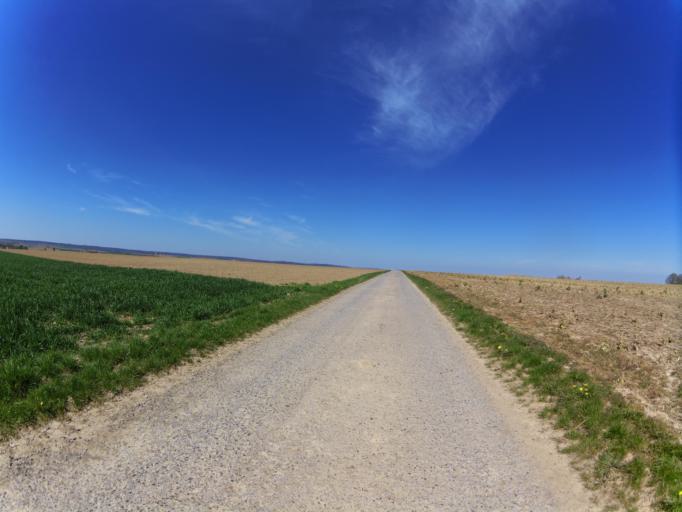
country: DE
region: Bavaria
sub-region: Regierungsbezirk Unterfranken
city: Eibelstadt
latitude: 49.6958
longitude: 9.9867
